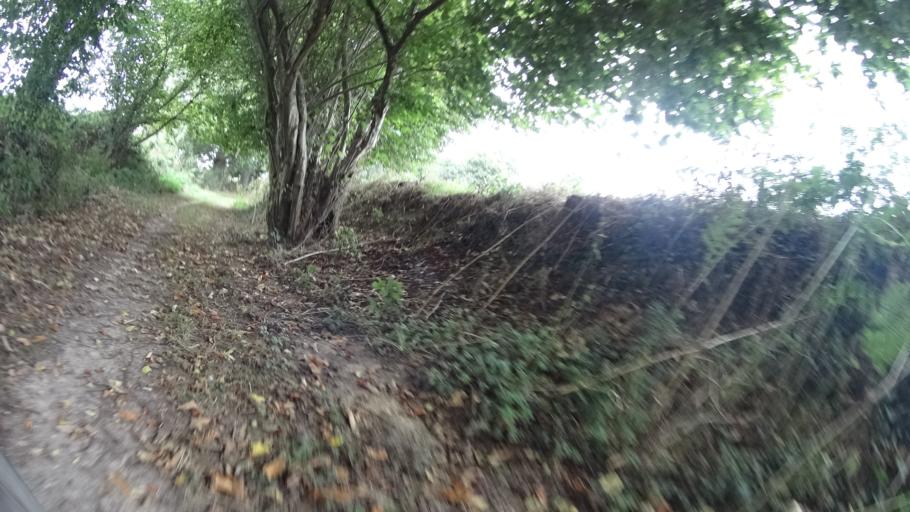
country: FR
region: Brittany
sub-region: Departement d'Ille-et-Vilaine
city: Geveze
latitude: 48.2297
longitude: -1.7817
